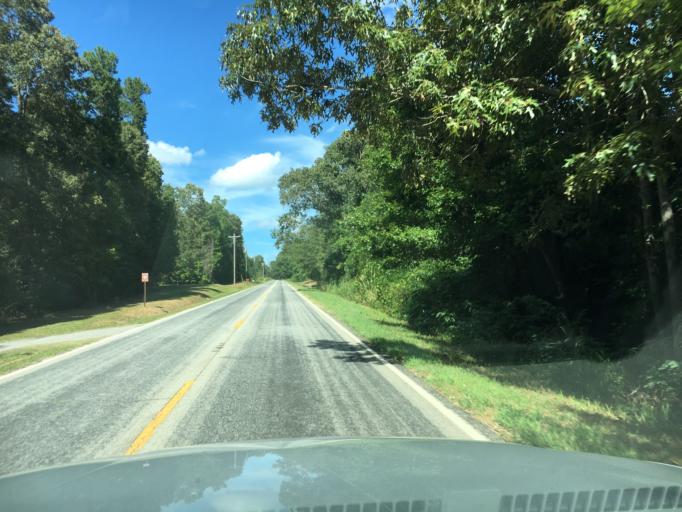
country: US
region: South Carolina
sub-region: Greenwood County
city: Ware Shoals
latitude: 34.4179
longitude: -82.2865
